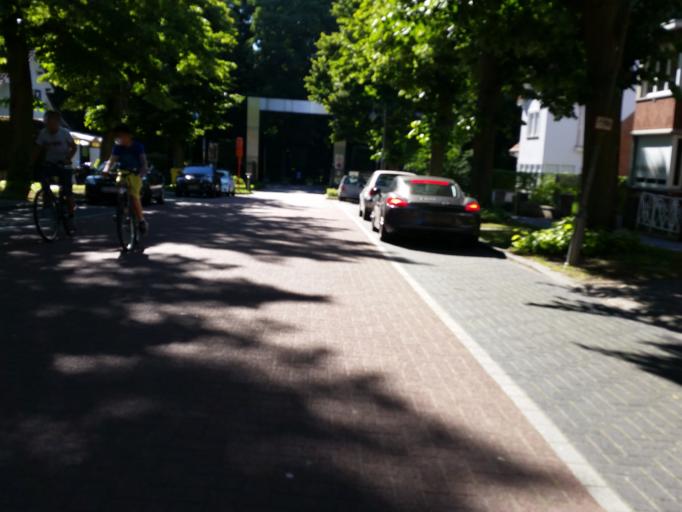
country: BE
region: Flanders
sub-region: Provincie Antwerpen
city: Mechelen
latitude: 51.0199
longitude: 4.4655
